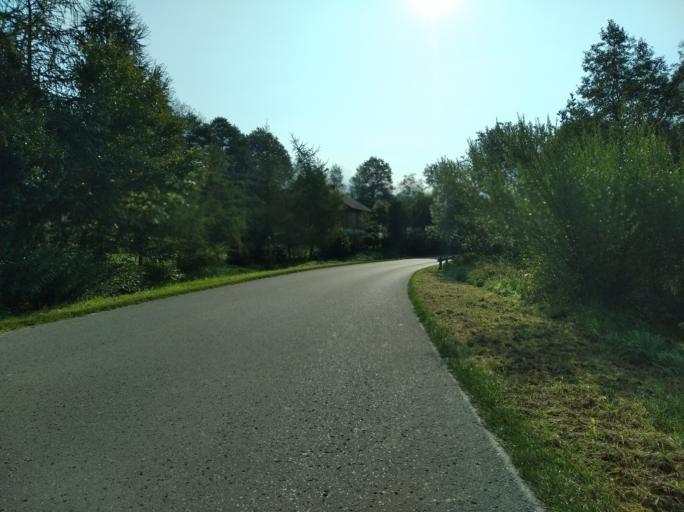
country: PL
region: Subcarpathian Voivodeship
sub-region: Powiat brzozowski
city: Nozdrzec
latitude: 49.7745
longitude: 22.1556
